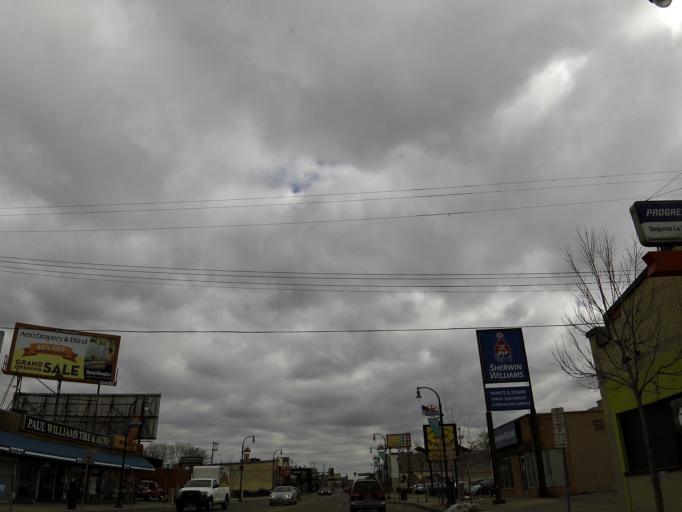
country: US
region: Minnesota
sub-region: Hennepin County
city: Minneapolis
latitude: 44.9484
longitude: -93.2865
